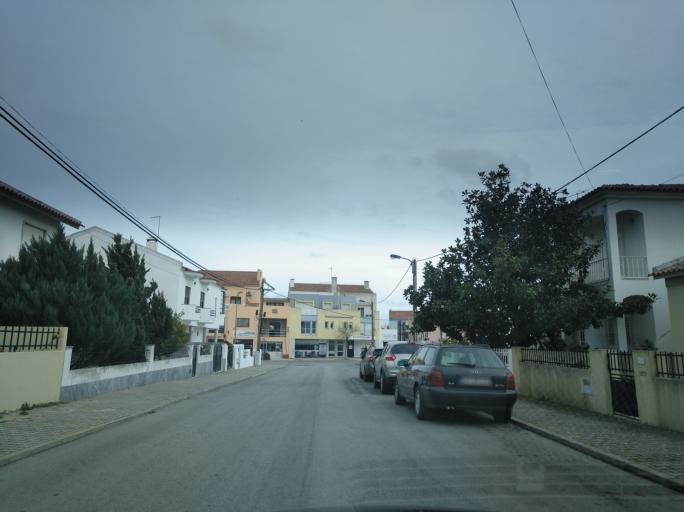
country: PT
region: Setubal
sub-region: Grandola
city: Grandola
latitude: 38.1821
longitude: -8.5679
